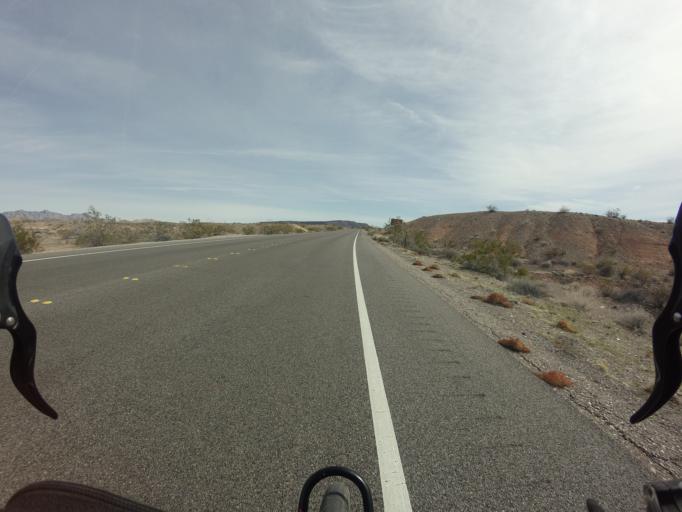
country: US
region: Nevada
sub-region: Clark County
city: Boulder City
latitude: 36.1560
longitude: -114.8225
